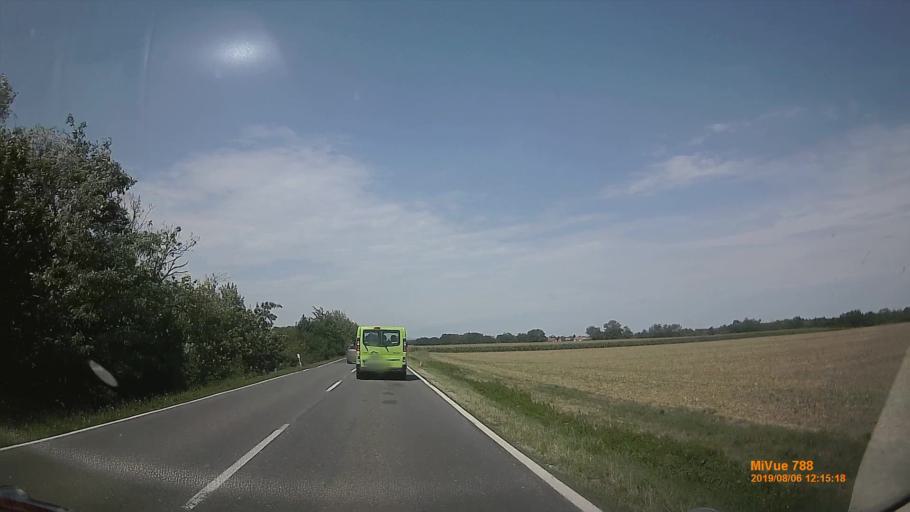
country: HU
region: Vas
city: Vasvar
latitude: 47.1476
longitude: 16.8200
